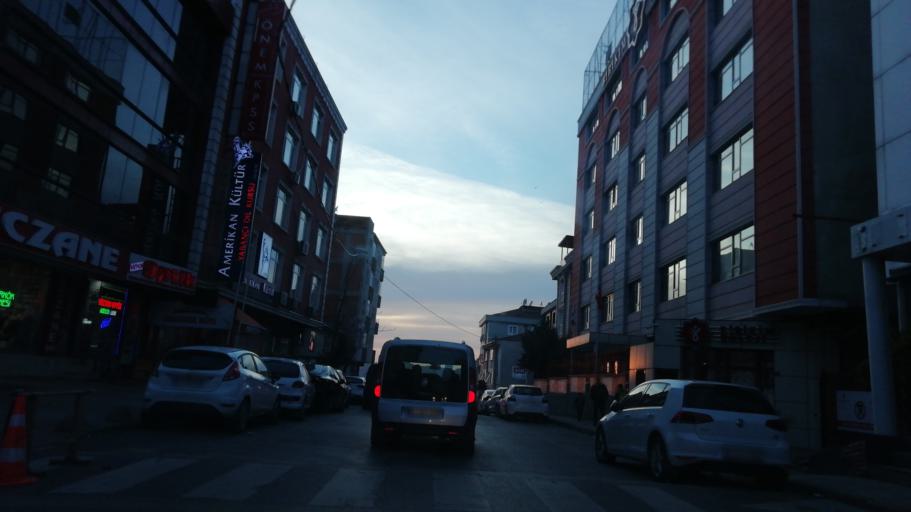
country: TR
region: Istanbul
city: Bagcilar
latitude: 41.0329
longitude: 28.8559
